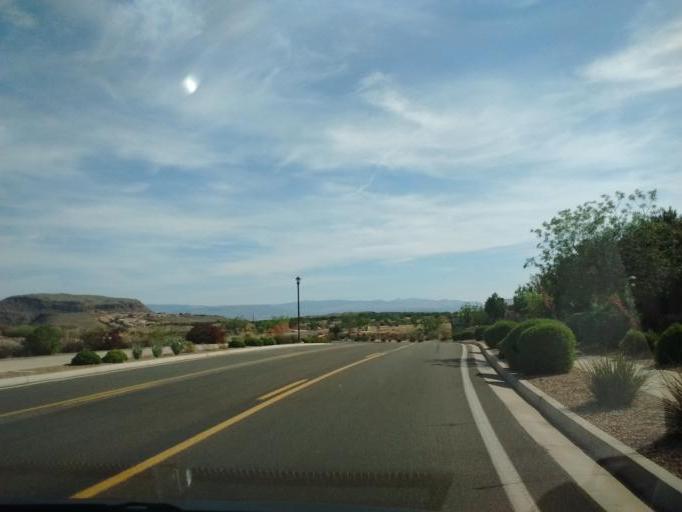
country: US
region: Utah
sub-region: Washington County
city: Washington
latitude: 37.1427
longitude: -113.4820
